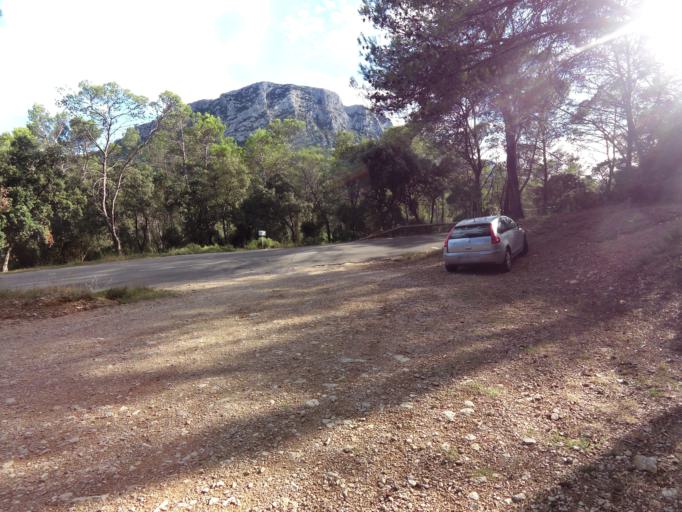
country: FR
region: Languedoc-Roussillon
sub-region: Departement de l'Herault
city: Saint-Mathieu-de-Treviers
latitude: 43.7911
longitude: 3.8211
